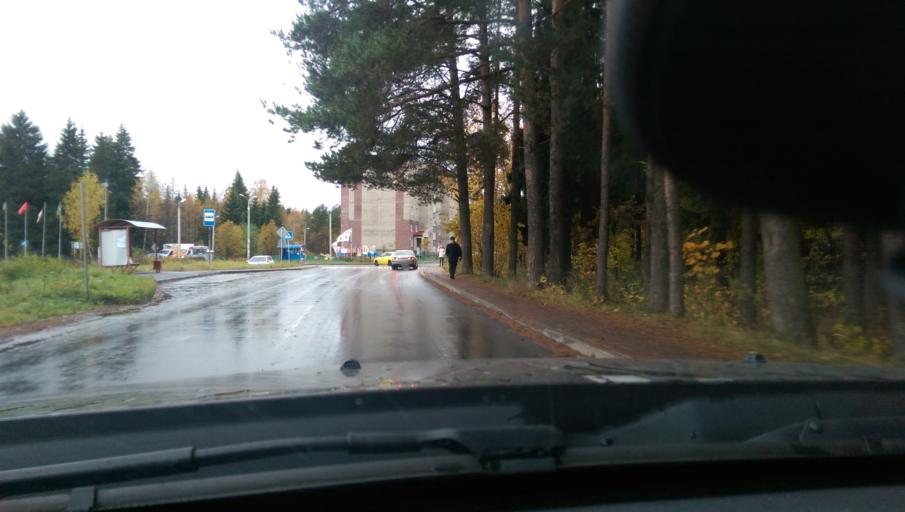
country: RU
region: Moskovskaya
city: Sofrino
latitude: 56.1295
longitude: 37.9133
